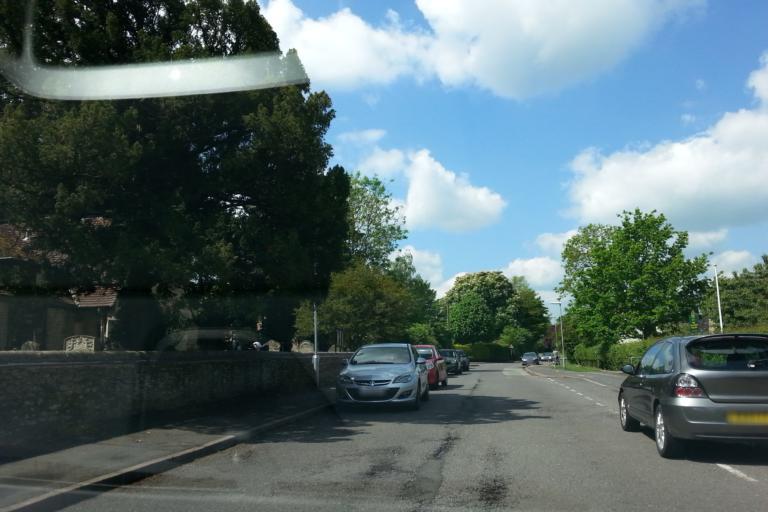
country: GB
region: England
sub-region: Cambridgeshire
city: Stilton
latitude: 52.4892
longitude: -0.2932
